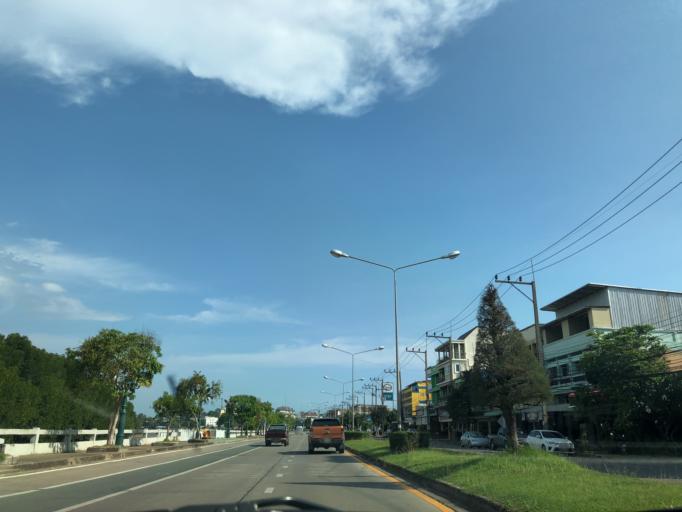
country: TH
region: Krabi
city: Krabi
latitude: 8.0716
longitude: 98.9166
